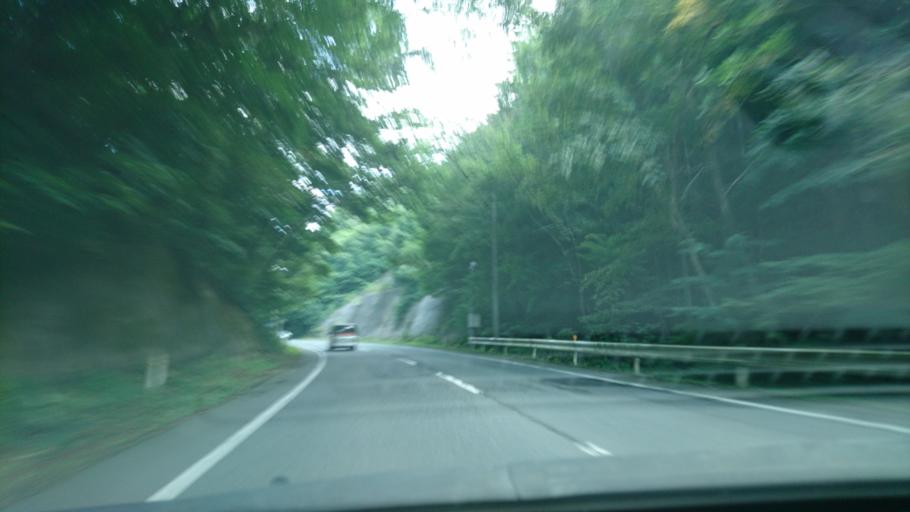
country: JP
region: Iwate
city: Mizusawa
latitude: 39.0611
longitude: 141.2245
